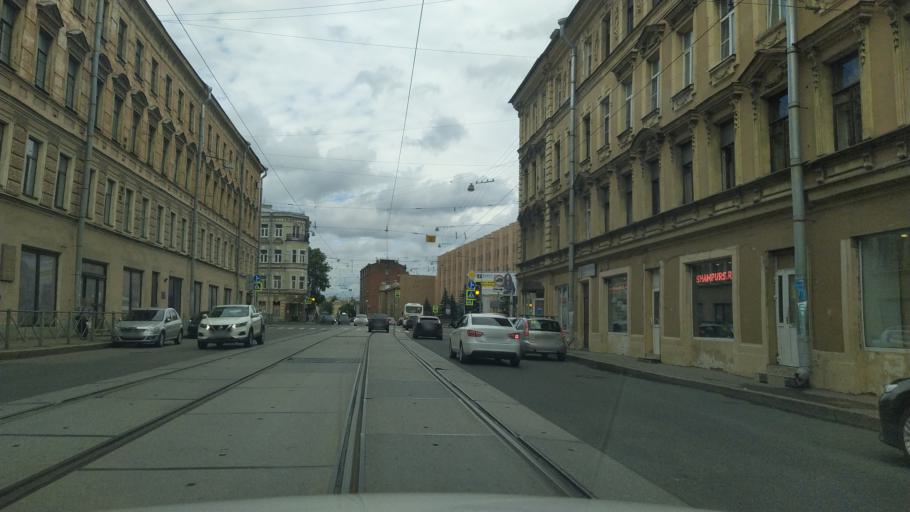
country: RU
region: Leningrad
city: Finlyandskiy
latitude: 59.9619
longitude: 30.3785
